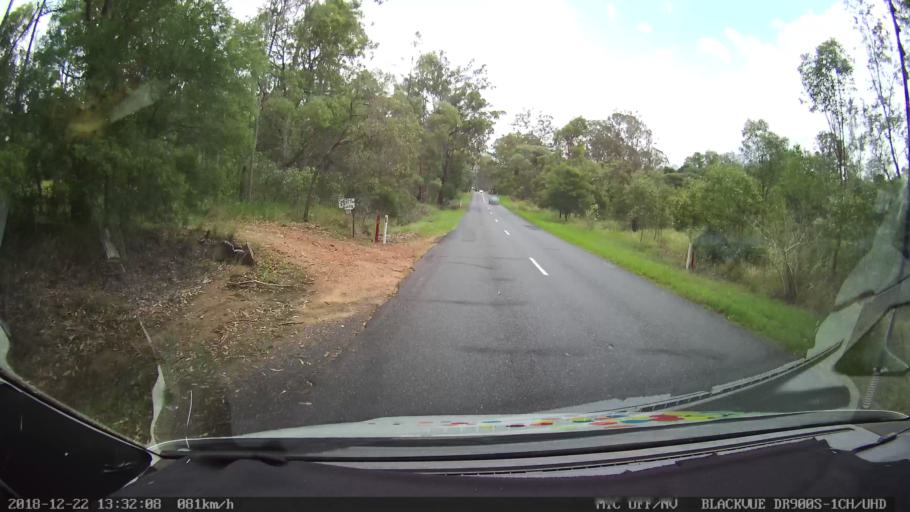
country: AU
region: New South Wales
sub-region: Clarence Valley
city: Coutts Crossing
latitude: -29.8598
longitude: 152.8448
